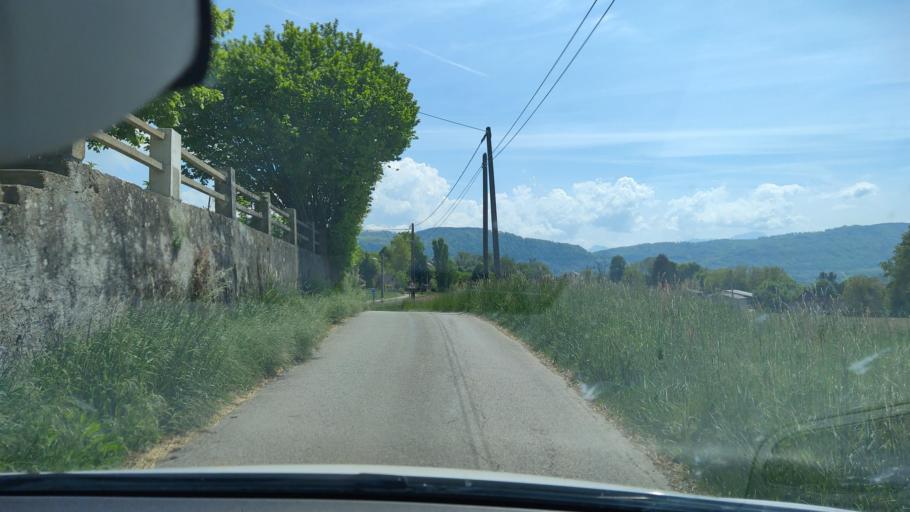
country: FR
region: Rhone-Alpes
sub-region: Departement de la Savoie
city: Domessin
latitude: 45.5242
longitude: 5.7151
